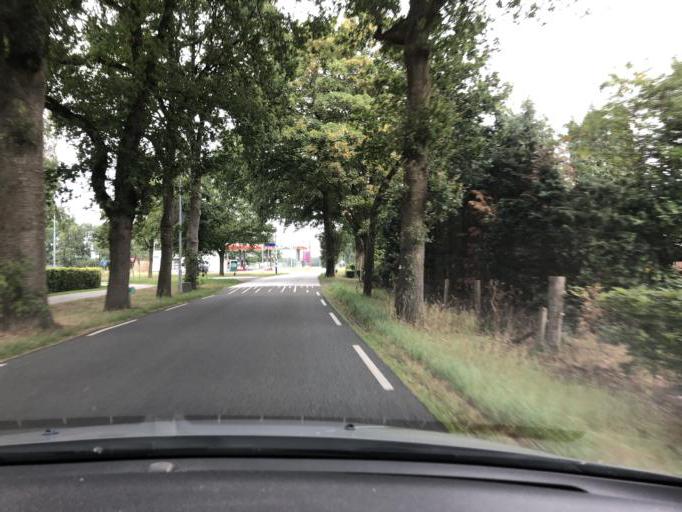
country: NL
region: Drenthe
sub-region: Gemeente Assen
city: Assen
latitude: 52.8836
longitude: 6.6489
